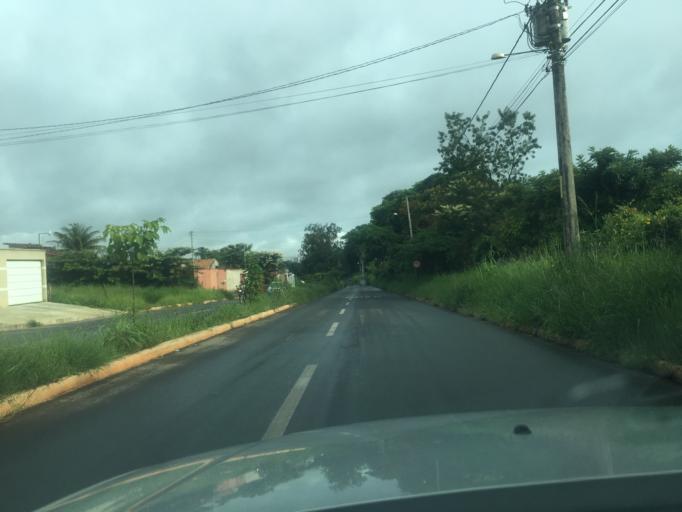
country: BR
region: Goias
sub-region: Aparecida De Goiania
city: Aparecida de Goiania
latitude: -16.8032
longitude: -49.2482
